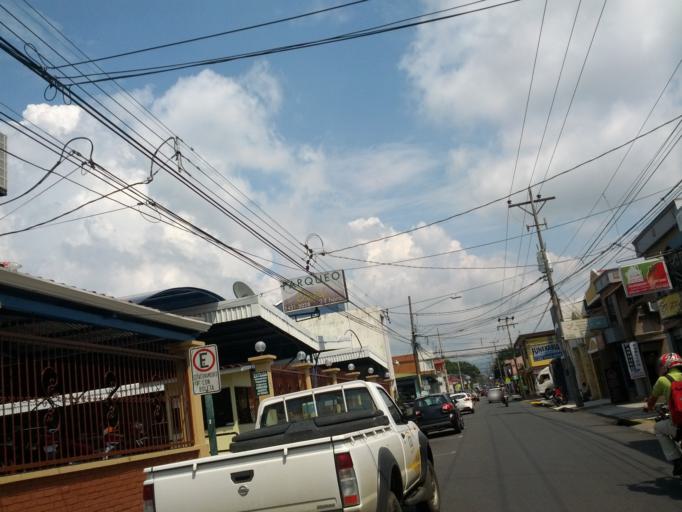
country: CR
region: Alajuela
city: Alajuela
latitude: 10.0188
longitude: -84.2138
